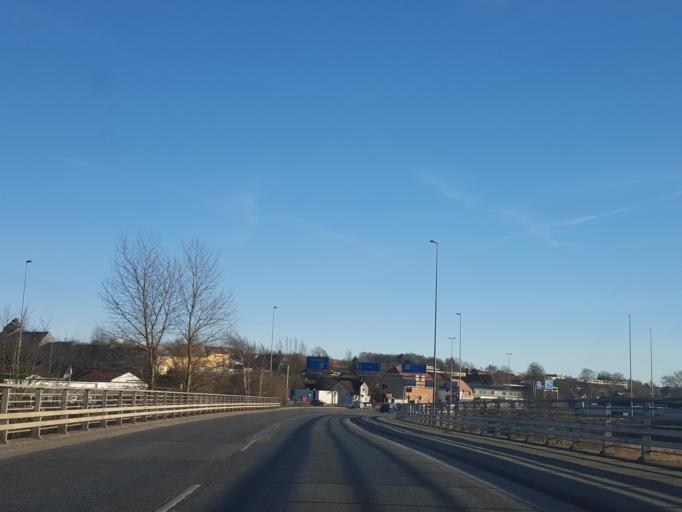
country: DK
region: North Denmark
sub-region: Alborg Kommune
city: Aalborg
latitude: 57.0284
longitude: 9.9260
